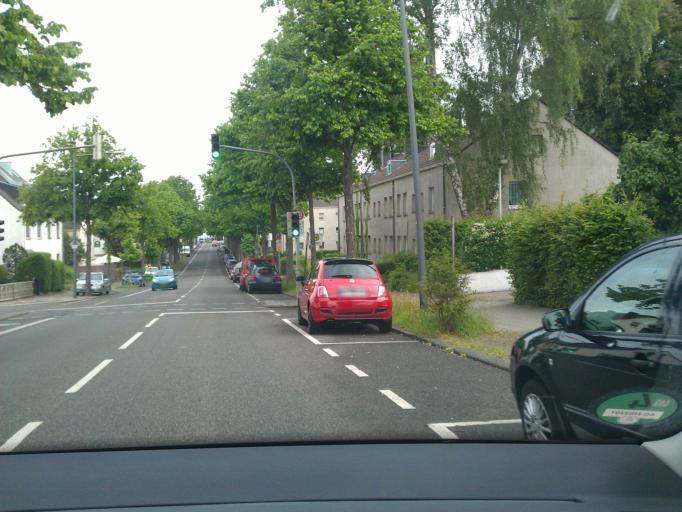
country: DE
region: North Rhine-Westphalia
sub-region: Regierungsbezirk Koln
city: Aachen
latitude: 50.7596
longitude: 6.0995
